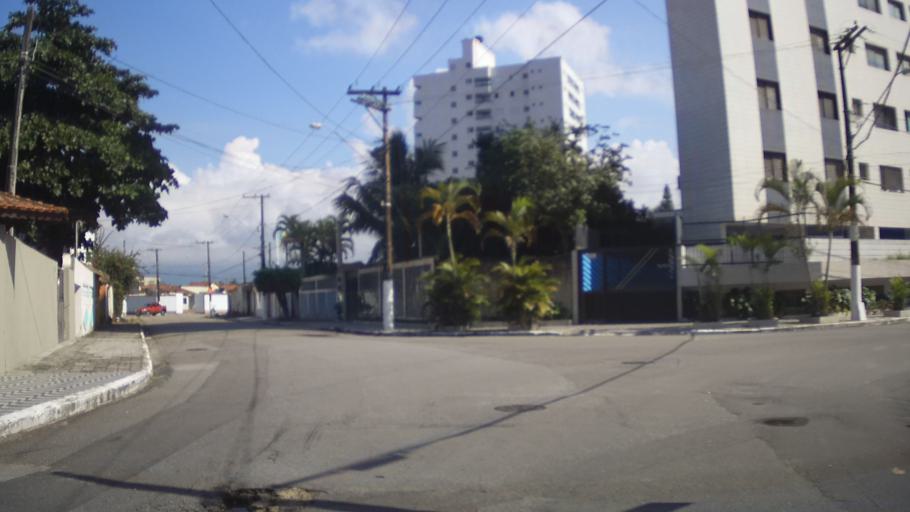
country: BR
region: Sao Paulo
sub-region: Praia Grande
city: Praia Grande
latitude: -24.0083
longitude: -46.4254
